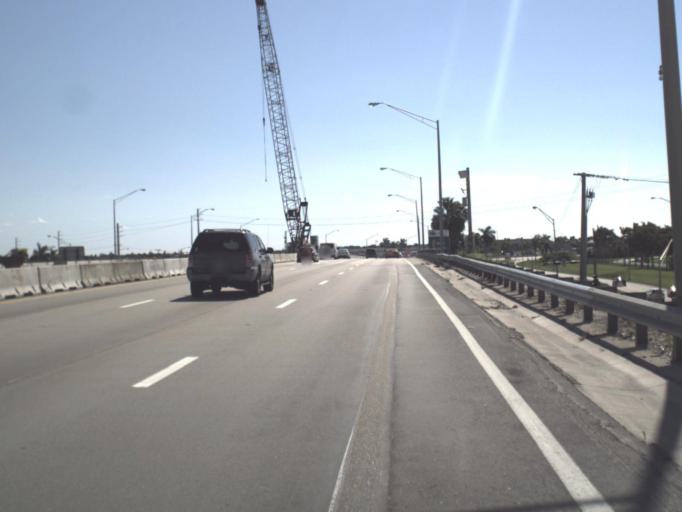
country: US
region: Florida
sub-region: Miami-Dade County
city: South Miami Heights
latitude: 25.5960
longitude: -80.3732
